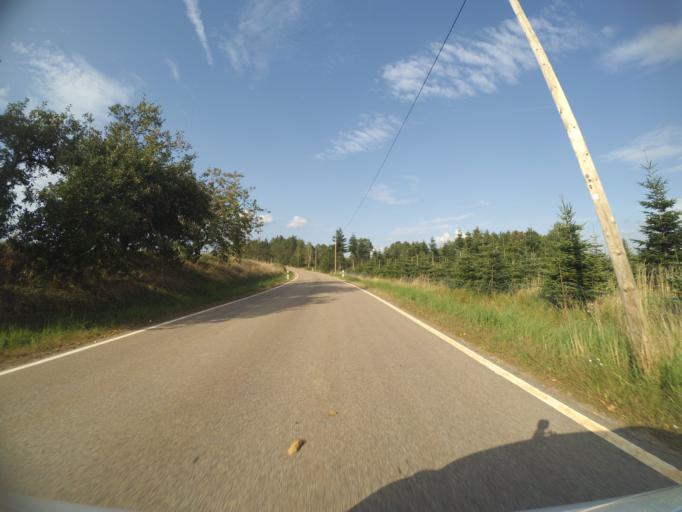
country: DE
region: Bavaria
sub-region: Upper Palatinate
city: Stulln
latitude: 49.4657
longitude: 12.1319
